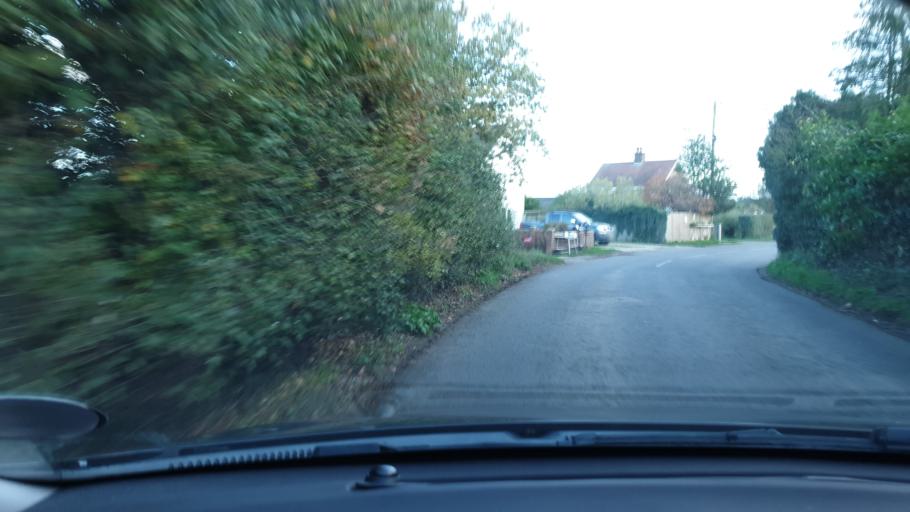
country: GB
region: England
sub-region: Essex
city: Little Clacton
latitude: 51.8985
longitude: 1.1449
